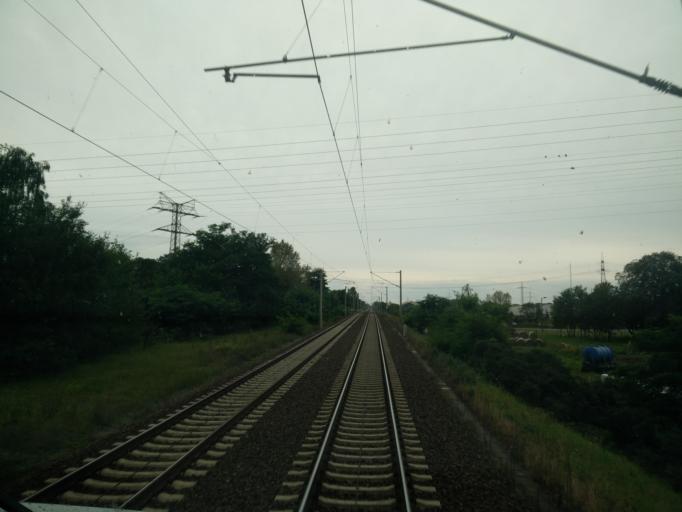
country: DE
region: Brandenburg
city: Brieselang
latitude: 52.5919
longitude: 12.9657
